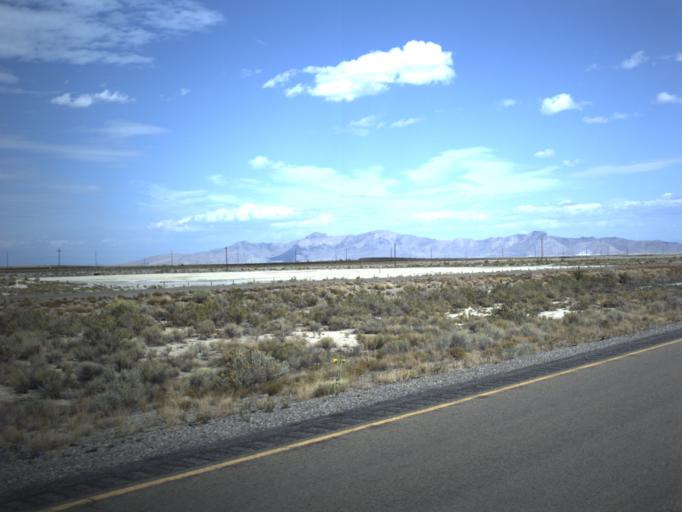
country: US
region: Utah
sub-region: Tooele County
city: Grantsville
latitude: 40.7540
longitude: -112.7369
